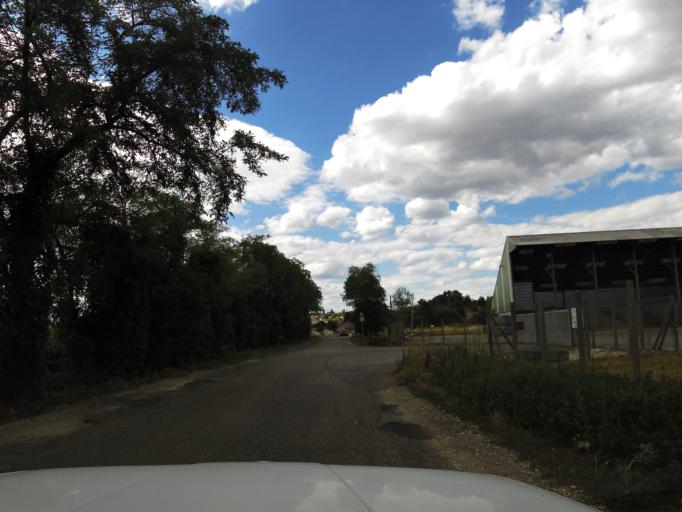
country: FR
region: Rhone-Alpes
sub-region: Departement de l'Ain
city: Meximieux
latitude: 45.8986
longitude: 5.2032
